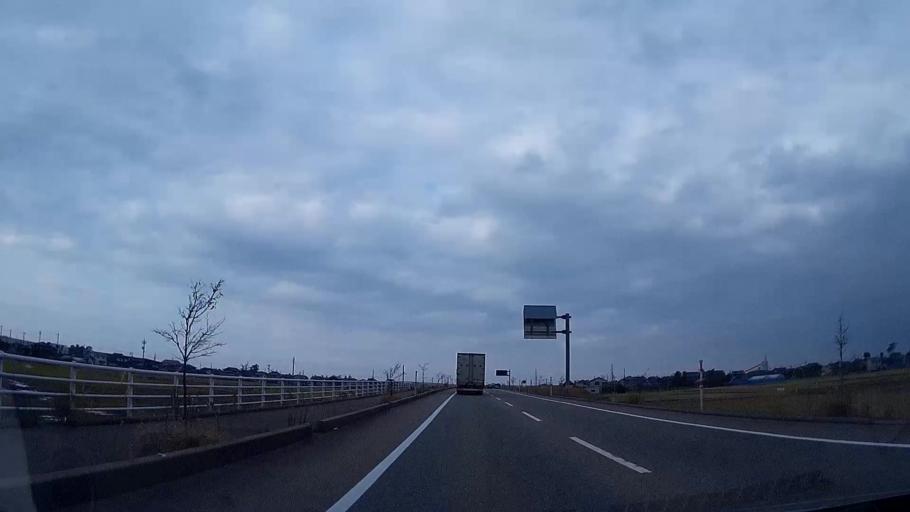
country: JP
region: Toyama
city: Nyuzen
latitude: 36.8946
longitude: 137.4442
